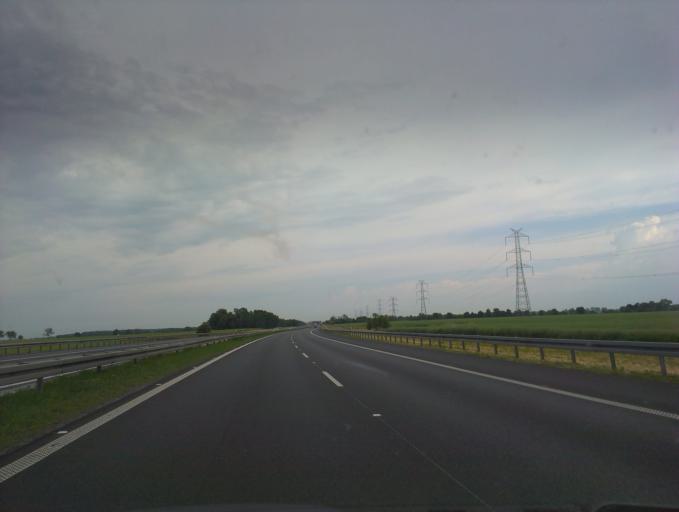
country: PL
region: Lower Silesian Voivodeship
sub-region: Powiat strzelinski
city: Wiazow
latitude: 50.8336
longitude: 17.2855
